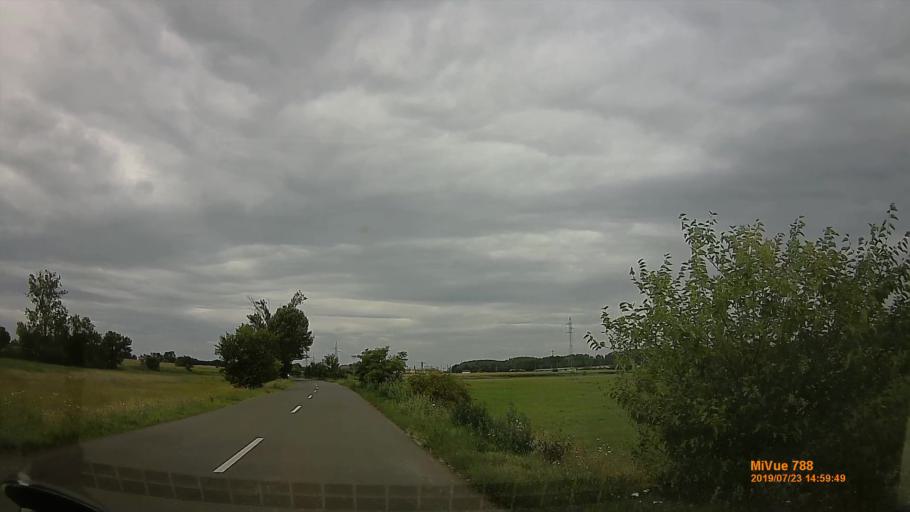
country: HU
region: Szabolcs-Szatmar-Bereg
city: Nyiregyhaza
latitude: 47.9241
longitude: 21.6774
